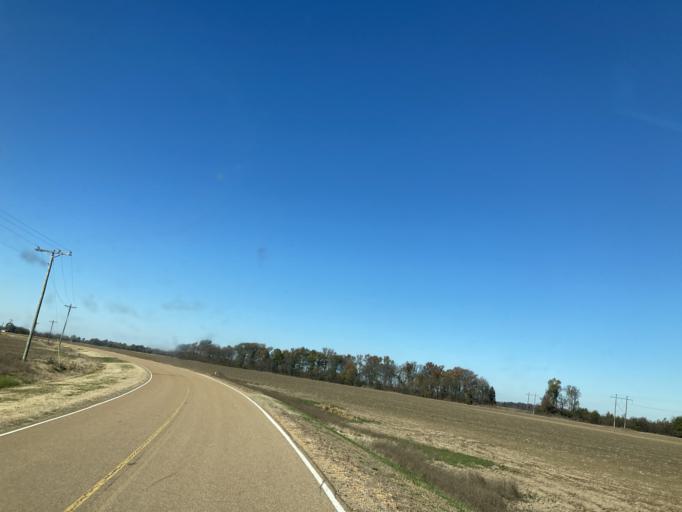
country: US
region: Mississippi
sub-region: Yazoo County
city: Yazoo City
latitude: 32.9158
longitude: -90.4478
